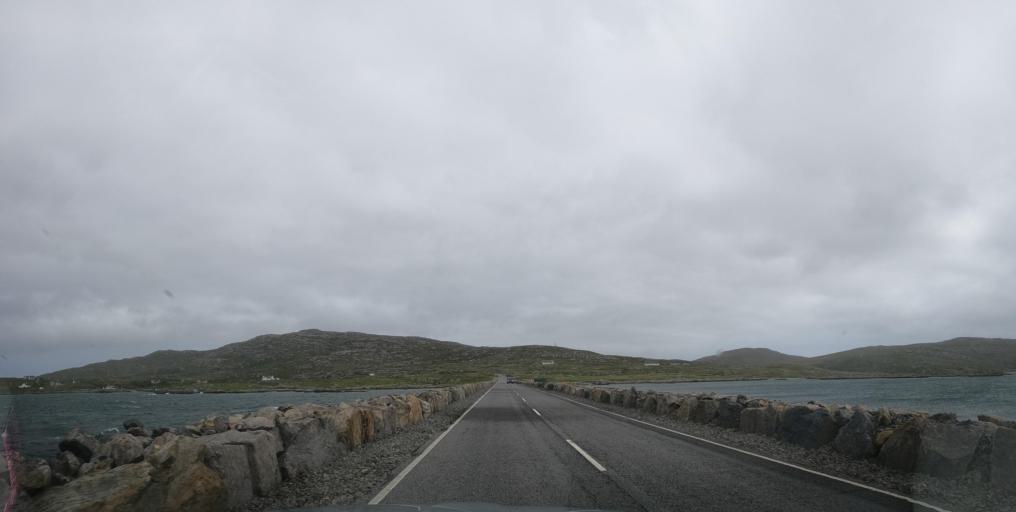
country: GB
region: Scotland
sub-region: Eilean Siar
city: Isle of South Uist
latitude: 57.1001
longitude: -7.3177
